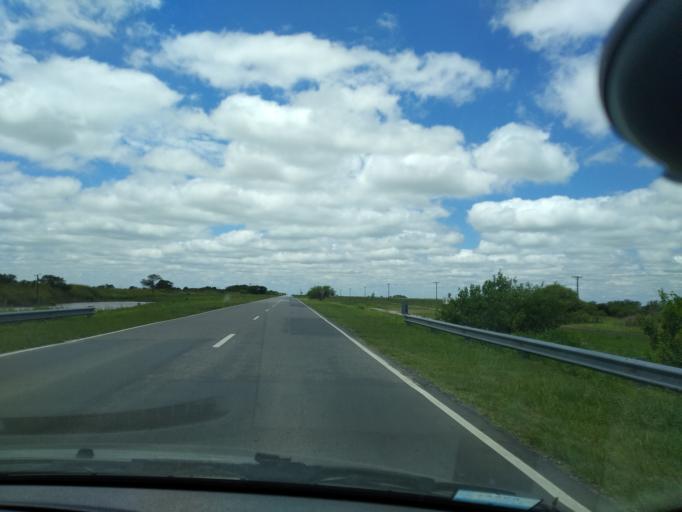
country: AR
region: Cordoba
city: Toledo
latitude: -31.6471
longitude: -64.0670
